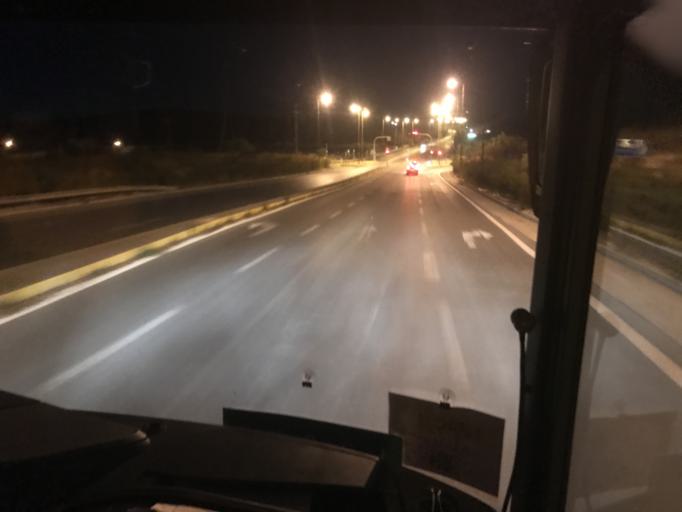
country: GR
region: Crete
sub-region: Nomos Irakleiou
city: Skalanion
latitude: 35.2815
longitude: 25.1803
